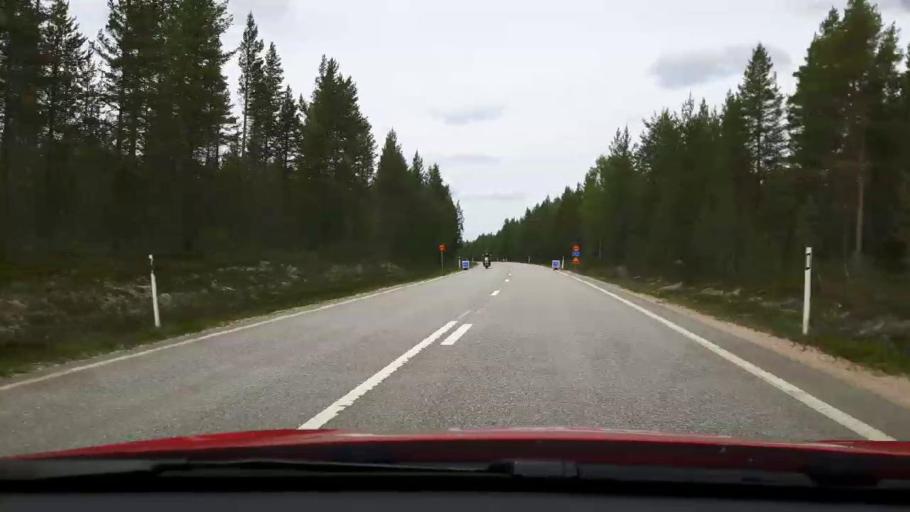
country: SE
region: Jaemtland
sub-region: Harjedalens Kommun
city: Sveg
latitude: 62.0749
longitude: 14.2687
